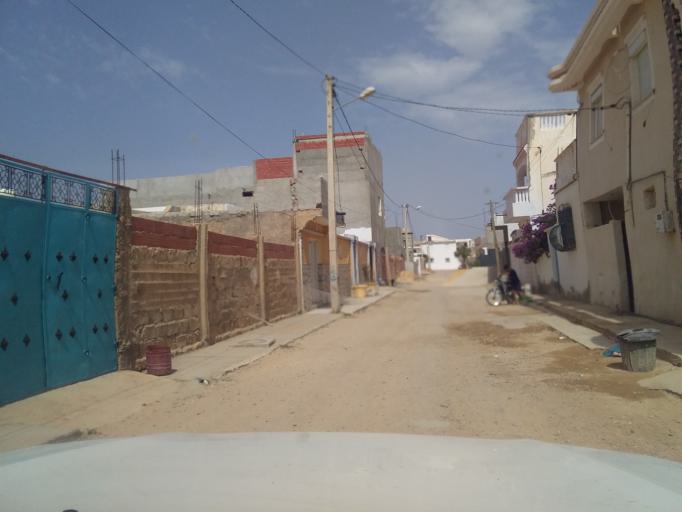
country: TN
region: Qabis
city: Matmata
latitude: 33.6155
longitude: 10.2808
